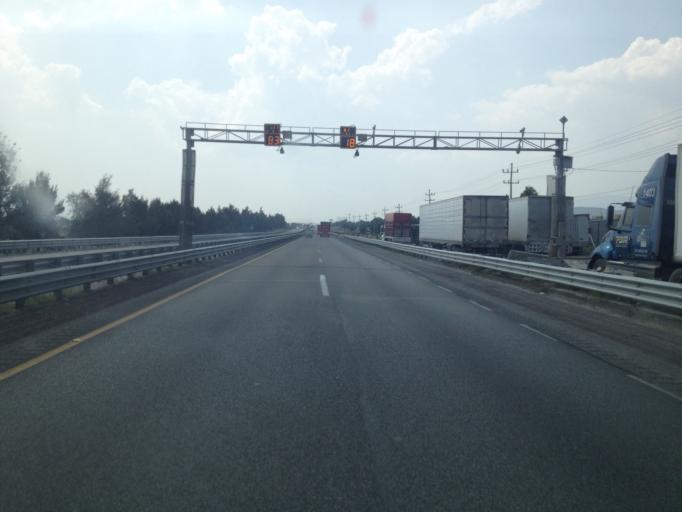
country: MX
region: Puebla
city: Cuacnopalan
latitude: 18.8326
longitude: -97.5098
